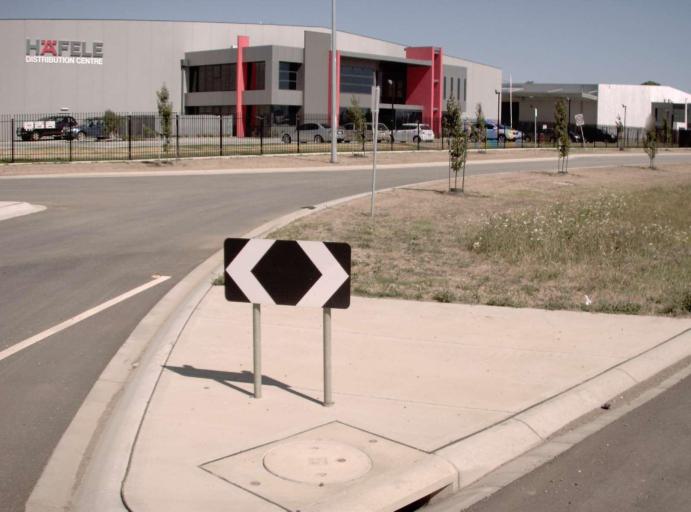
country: AU
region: Victoria
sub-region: Frankston
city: Sandhurst
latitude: -38.0511
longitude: 145.2082
